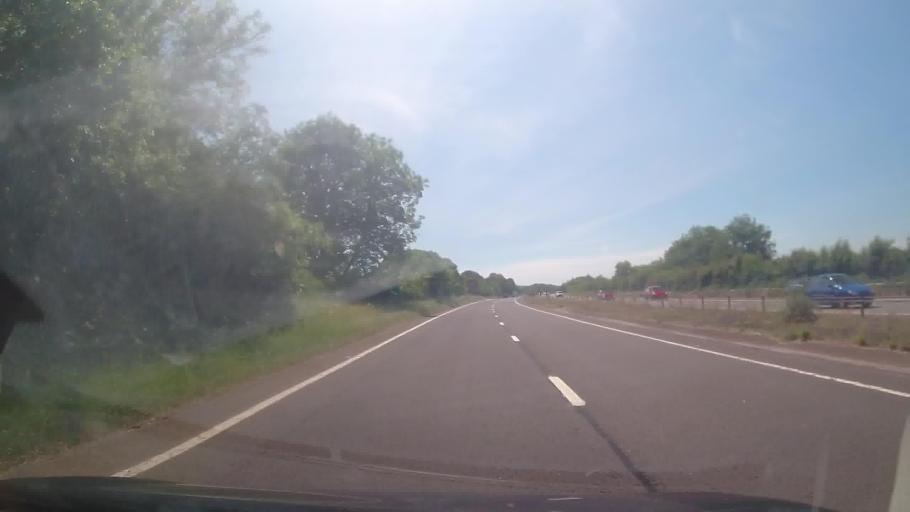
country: GB
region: England
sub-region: Devon
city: Ottery St Mary
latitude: 50.7846
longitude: -3.2406
